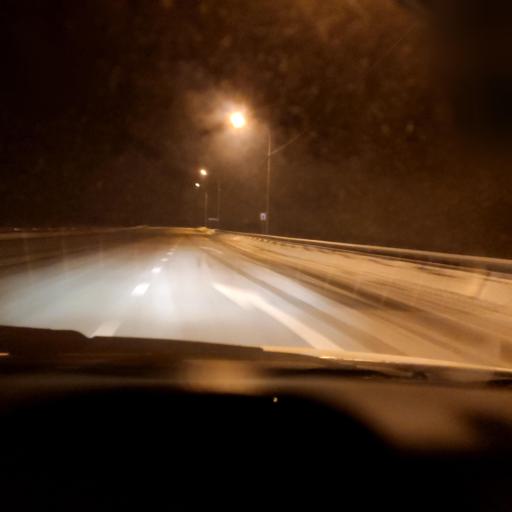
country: RU
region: Kursk
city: Fatezh
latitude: 52.0984
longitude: 35.8179
